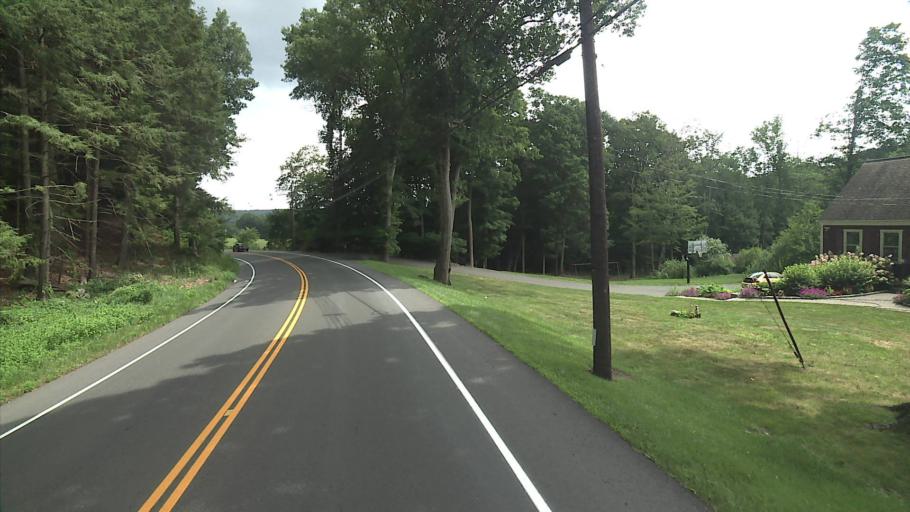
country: US
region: Connecticut
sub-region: New Haven County
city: Heritage Village
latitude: 41.5029
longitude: -73.2304
